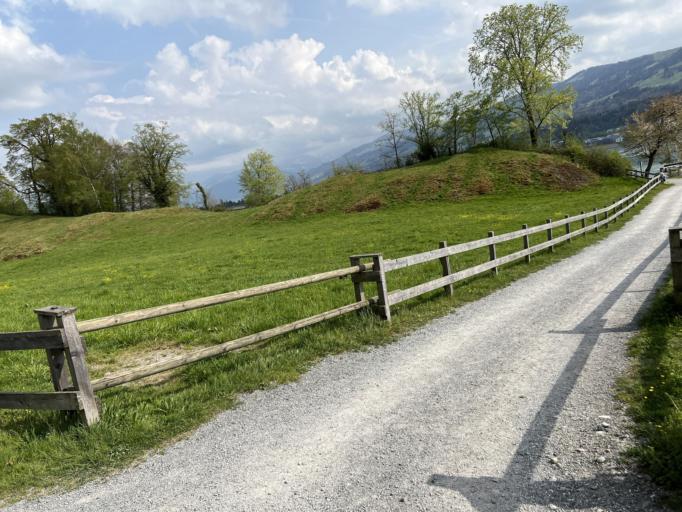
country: CH
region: Schwyz
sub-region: Bezirk Hoefe
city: Freienbach
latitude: 47.2167
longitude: 8.7785
